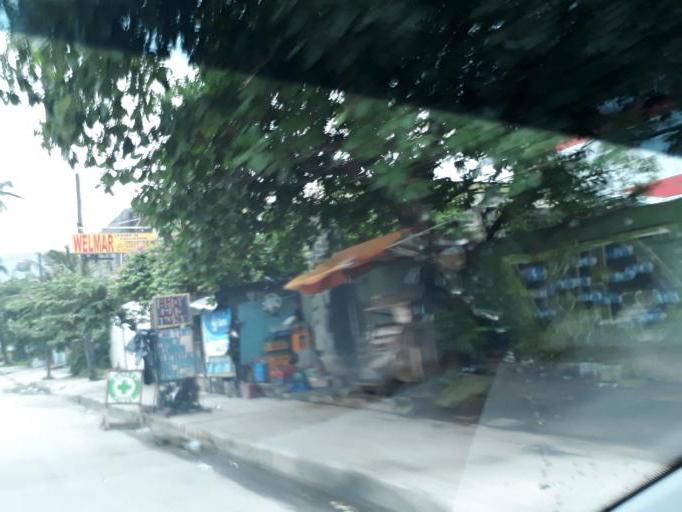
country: PH
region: Calabarzon
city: Del Monte
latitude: 14.6426
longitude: 121.0003
